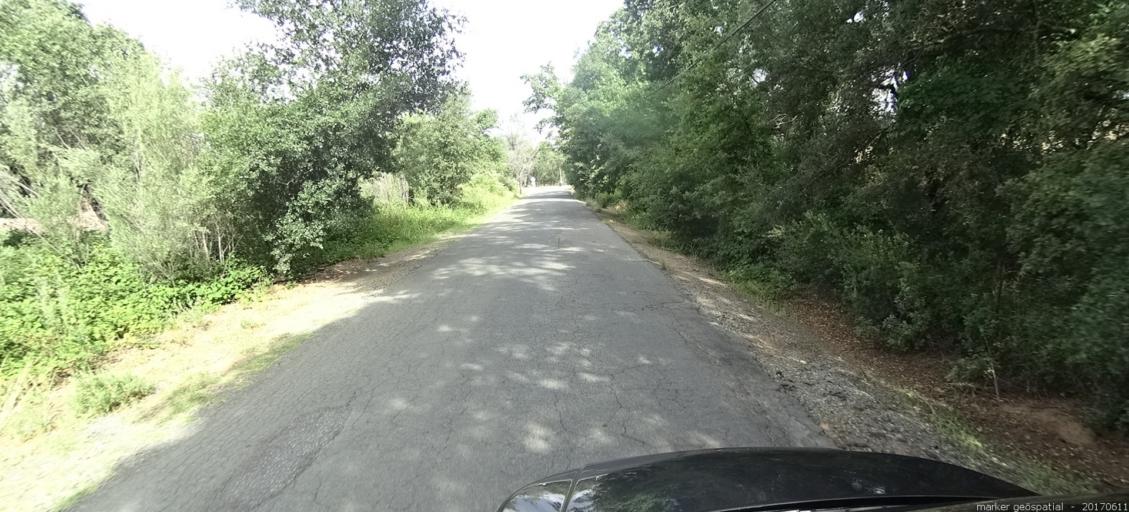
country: US
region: California
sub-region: Butte County
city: Oroville East
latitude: 39.4830
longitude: -121.4999
